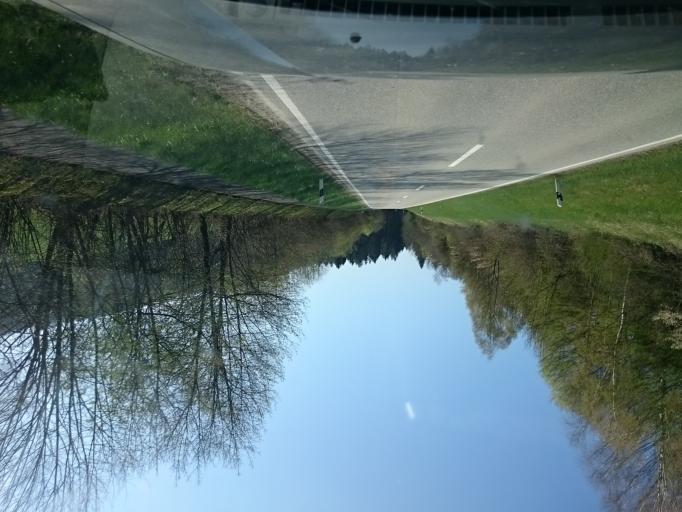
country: DE
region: Bavaria
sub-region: Upper Bavaria
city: Grossweil
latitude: 47.6632
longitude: 11.2707
